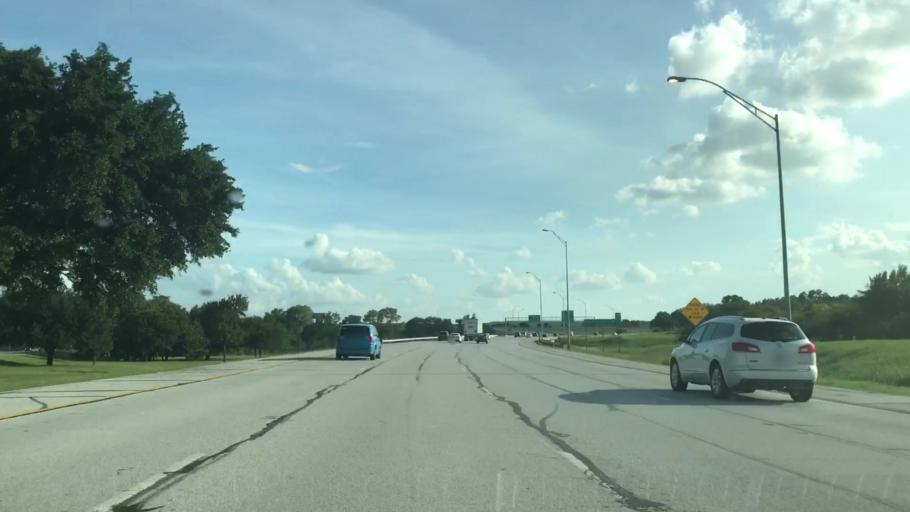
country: US
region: Texas
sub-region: Tarrant County
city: Euless
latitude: 32.8446
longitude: -97.0410
